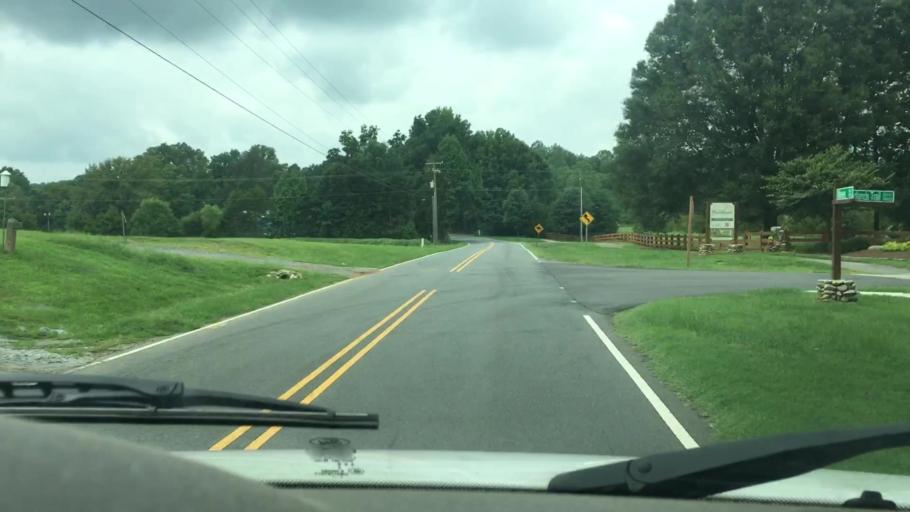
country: US
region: North Carolina
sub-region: Gaston County
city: Davidson
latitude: 35.4569
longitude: -80.8121
